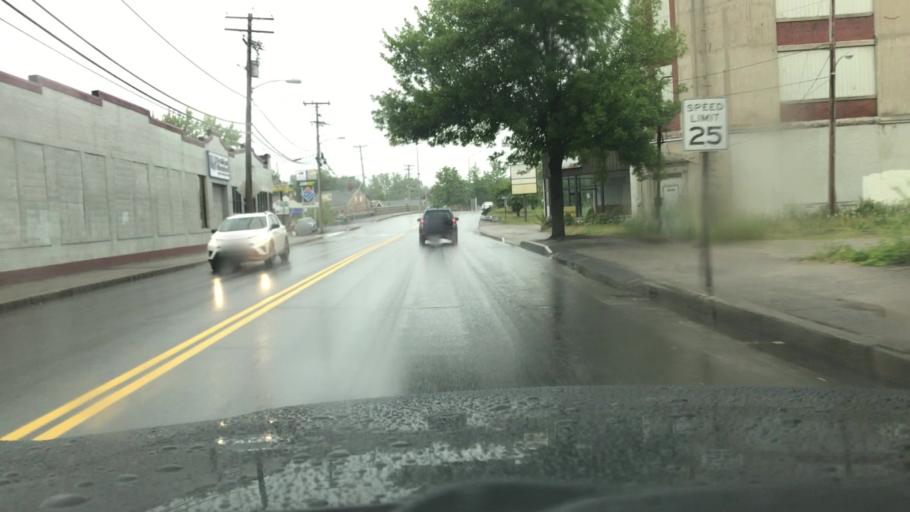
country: US
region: Maine
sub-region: York County
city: Biddeford
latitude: 43.4968
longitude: -70.4562
